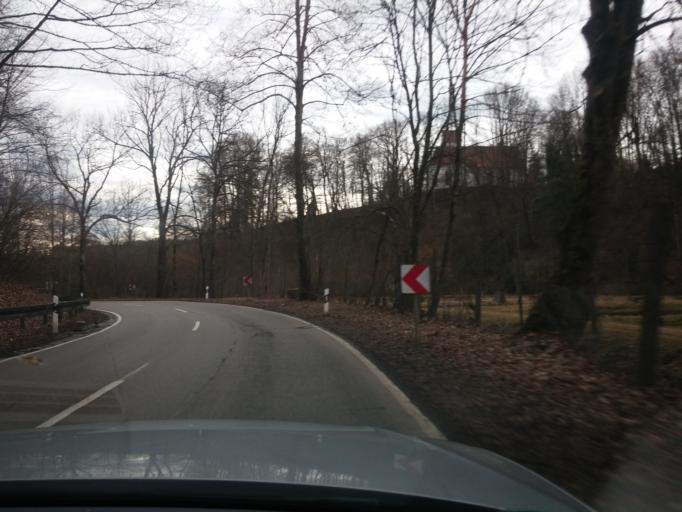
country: DE
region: Bavaria
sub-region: Upper Bavaria
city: Moosach
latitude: 48.0368
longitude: 11.8656
